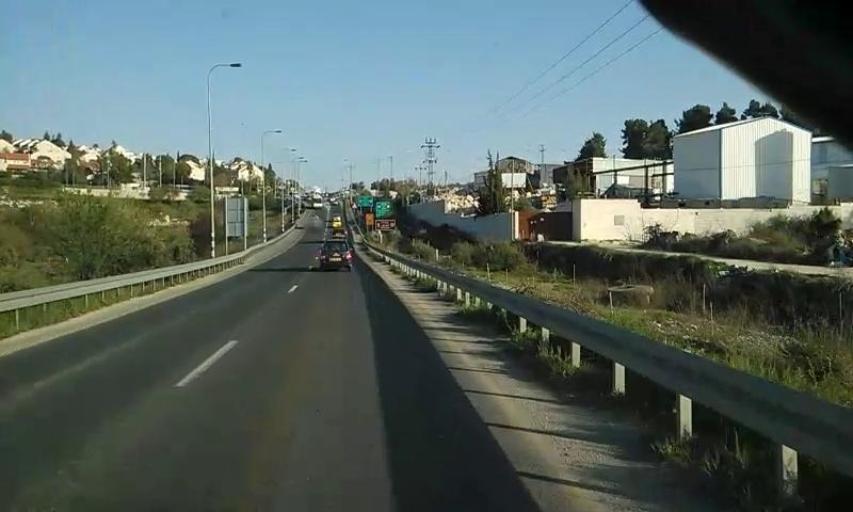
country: PS
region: West Bank
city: Jurat ash Sham`ah
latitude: 31.6494
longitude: 35.1453
